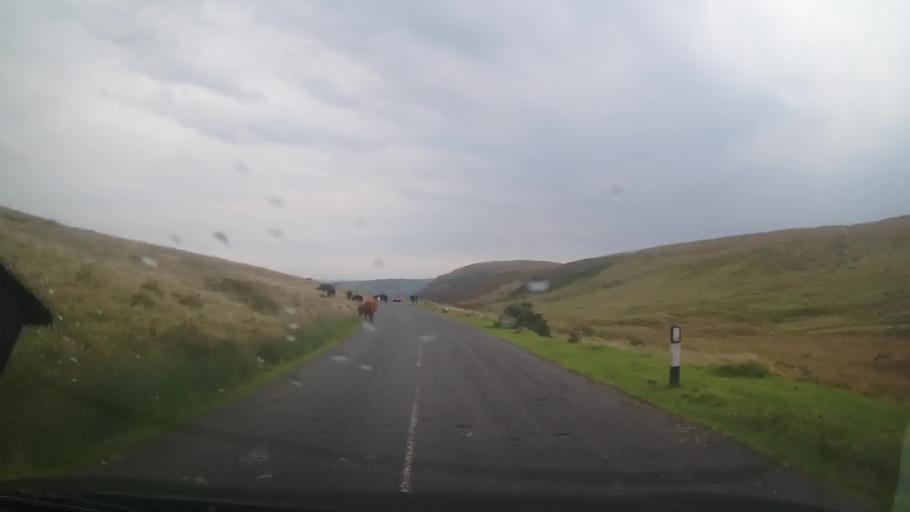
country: GB
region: Wales
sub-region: Sir Powys
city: Rhayader
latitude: 52.3170
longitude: -3.5717
